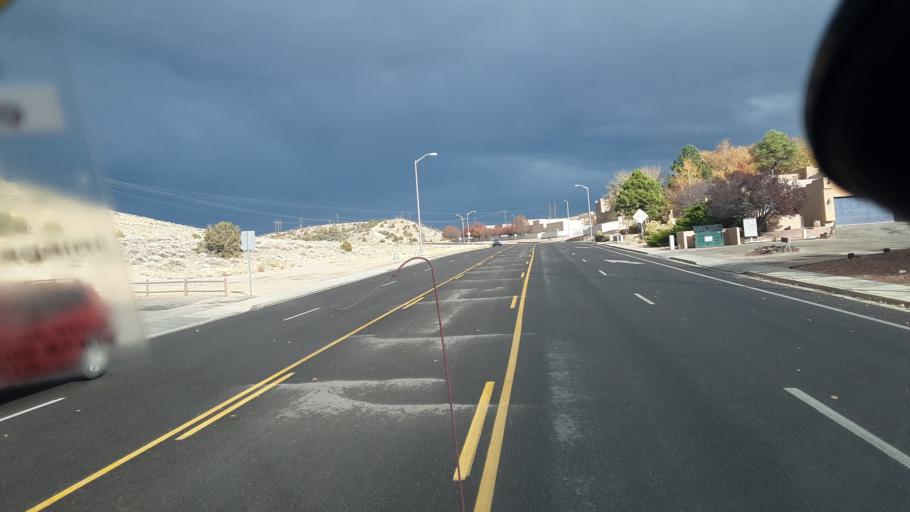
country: US
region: New Mexico
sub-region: San Juan County
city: Farmington
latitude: 36.7616
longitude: -108.1919
